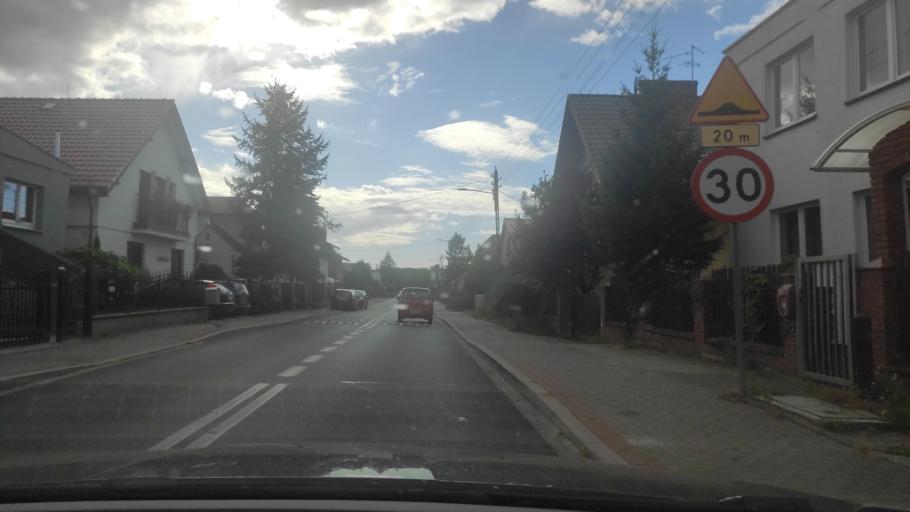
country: PL
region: Greater Poland Voivodeship
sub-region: Powiat poznanski
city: Swarzedz
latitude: 52.4093
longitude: 17.0560
